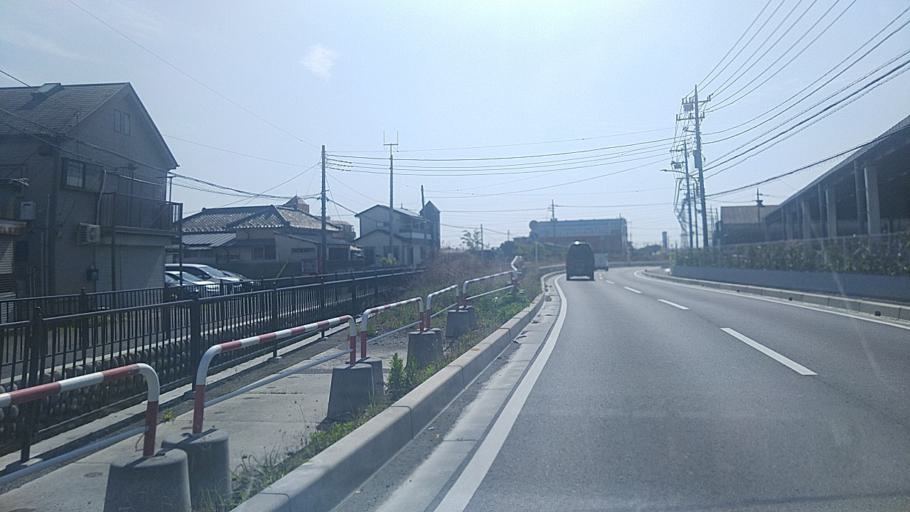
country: JP
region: Saitama
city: Koshigaya
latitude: 35.8714
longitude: 139.7673
